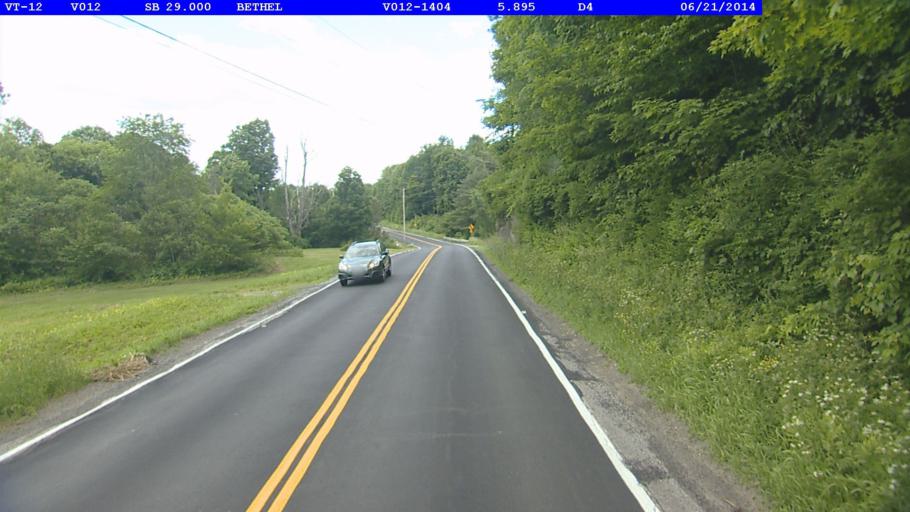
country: US
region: Vermont
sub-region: Orange County
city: Randolph
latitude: 43.8805
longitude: -72.6465
